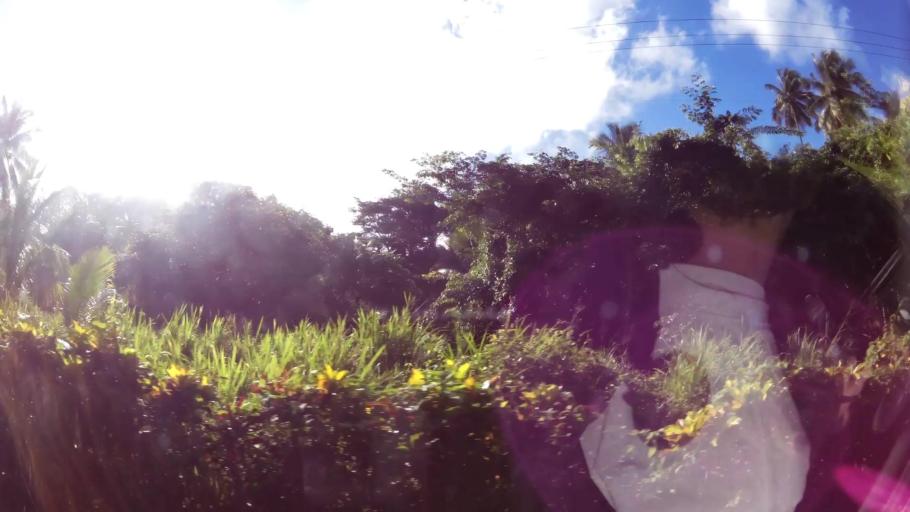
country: DM
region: Saint Andrew
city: Calibishie
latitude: 15.5931
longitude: -61.3848
